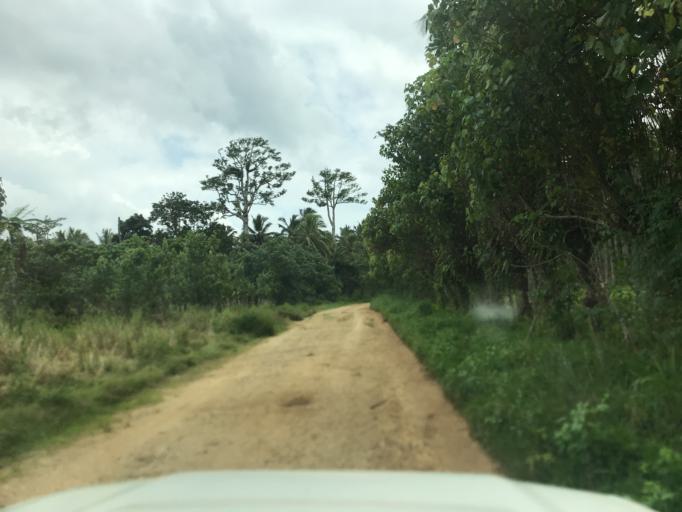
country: VU
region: Sanma
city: Port-Olry
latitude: -15.1873
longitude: 167.0192
